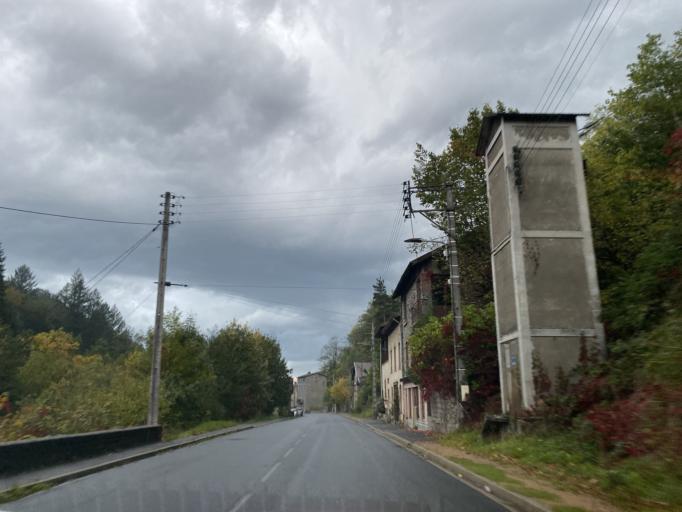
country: FR
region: Auvergne
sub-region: Departement du Puy-de-Dome
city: La Monnerie-le-Montel
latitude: 45.8677
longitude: 3.6144
